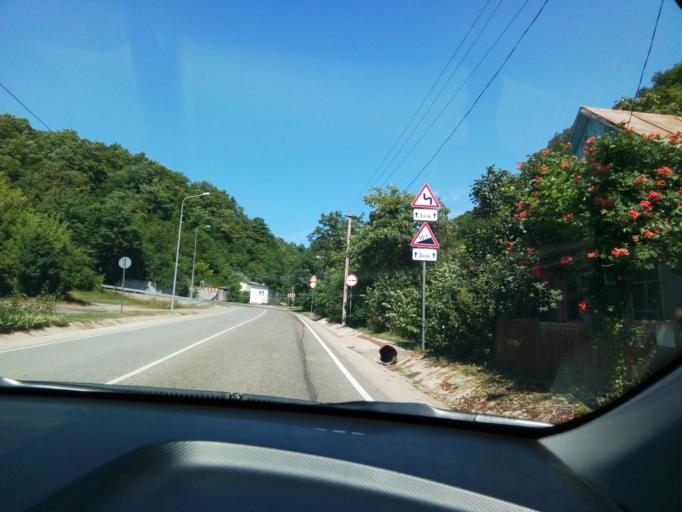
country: RU
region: Krasnodarskiy
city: Khadyzhensk
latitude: 44.3285
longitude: 39.2952
